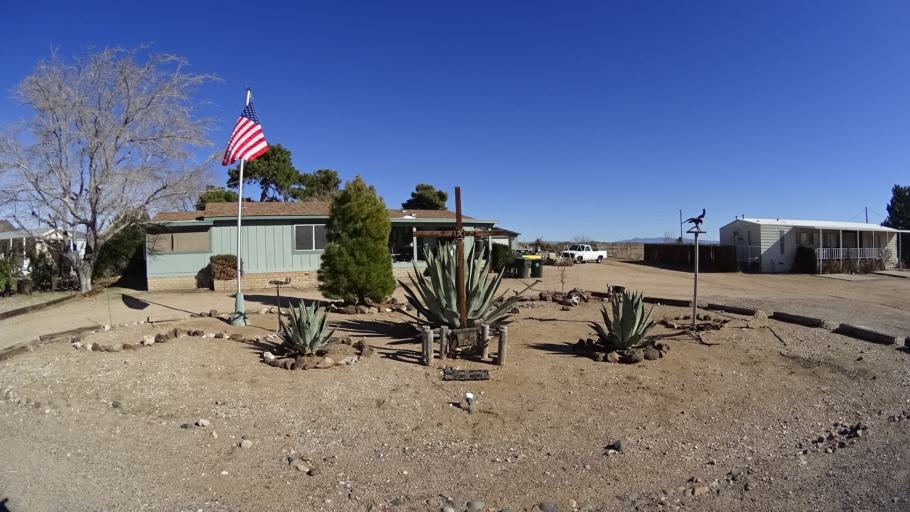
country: US
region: Arizona
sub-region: Mohave County
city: New Kingman-Butler
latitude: 35.2726
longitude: -114.0475
